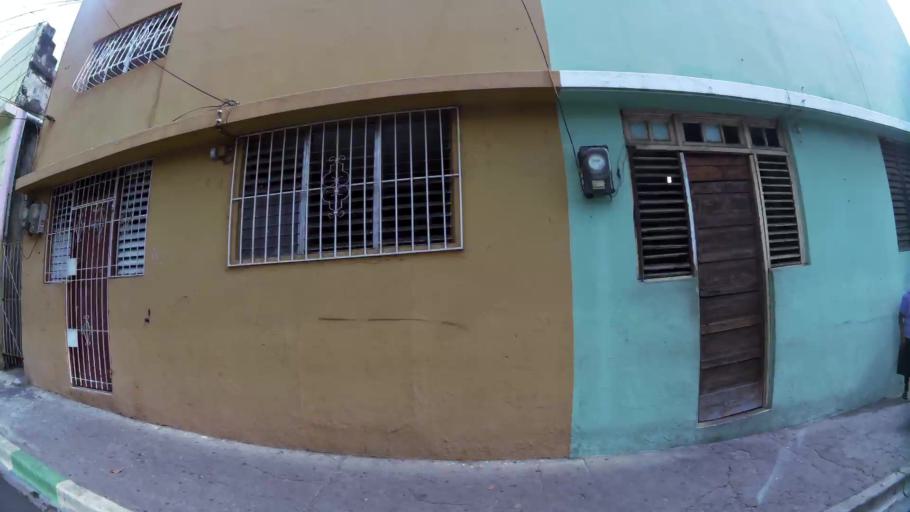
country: DO
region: Nacional
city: San Carlos
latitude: 18.4775
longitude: -69.8931
